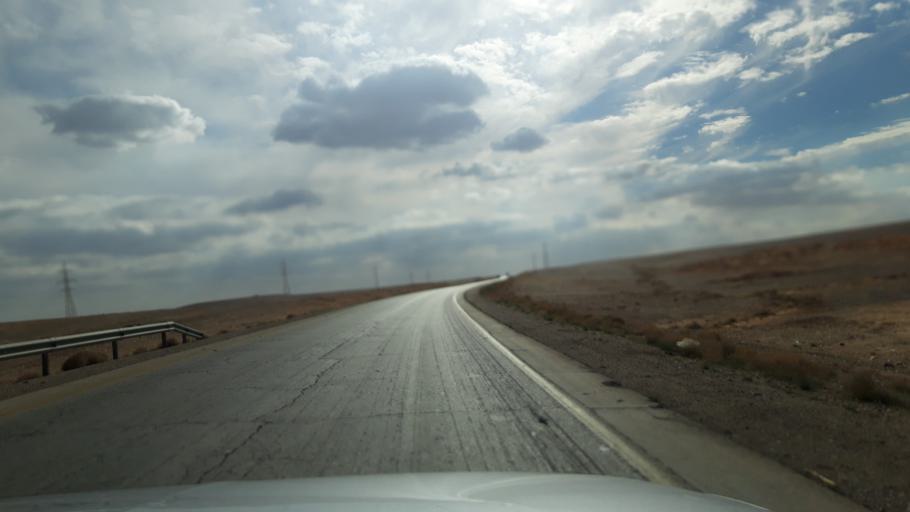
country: JO
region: Amman
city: Al Azraq ash Shamali
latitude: 31.7429
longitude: 36.5337
